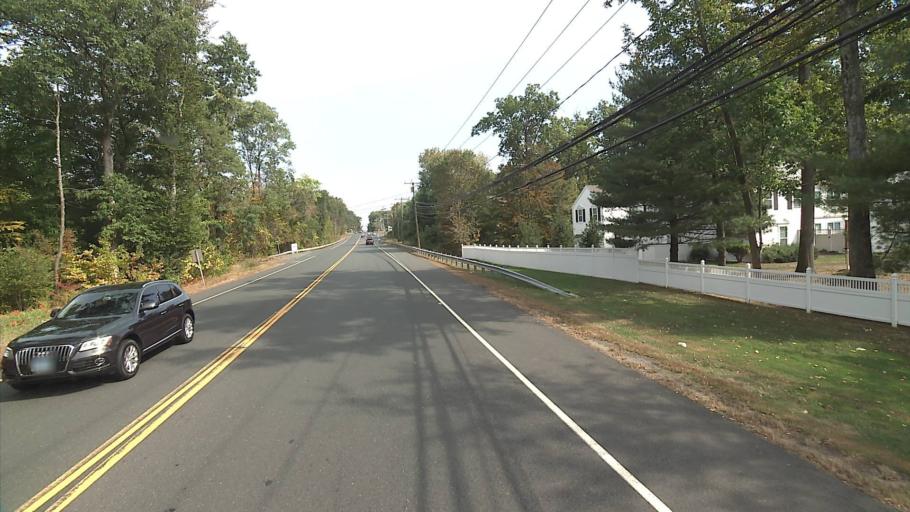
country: US
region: Connecticut
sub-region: Hartford County
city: Farmington
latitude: 41.7092
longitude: -72.8127
